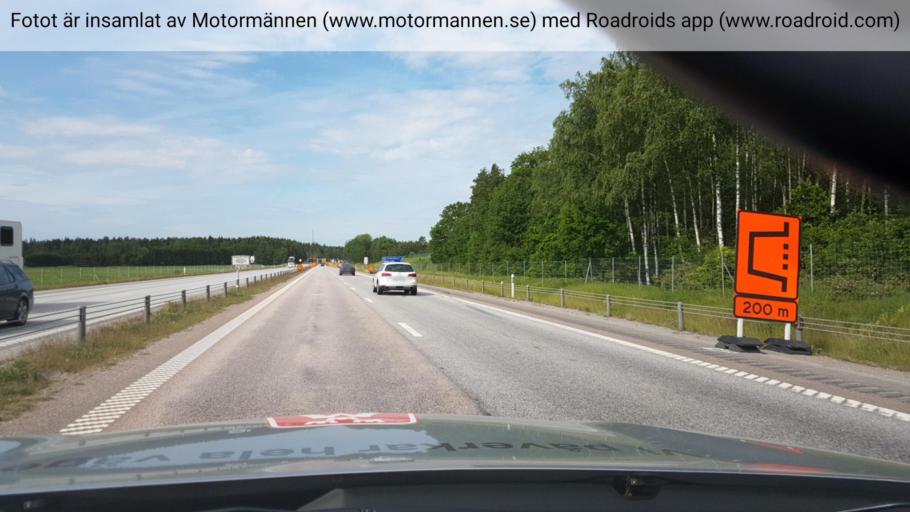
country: SE
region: Vaestmanland
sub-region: Hallstahammars Kommun
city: Kolback
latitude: 59.5847
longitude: 16.3709
